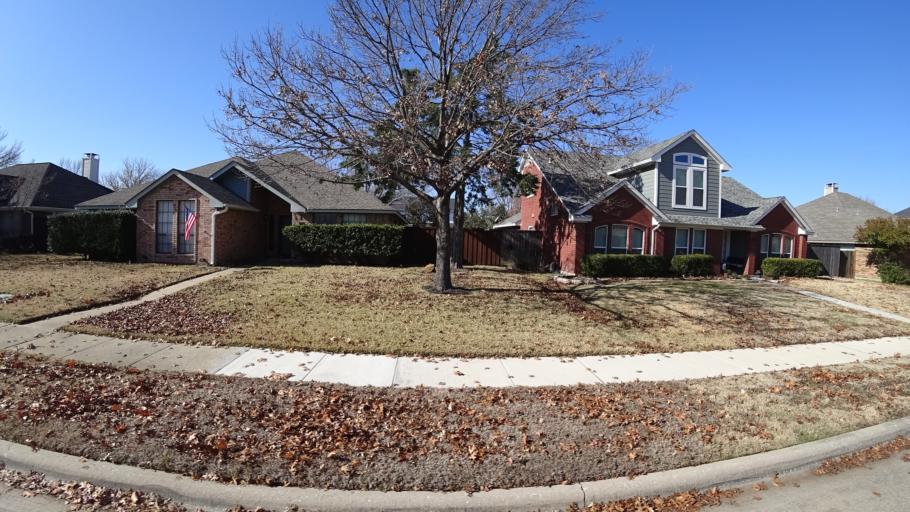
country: US
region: Texas
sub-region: Denton County
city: Lewisville
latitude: 33.0123
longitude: -97.0139
